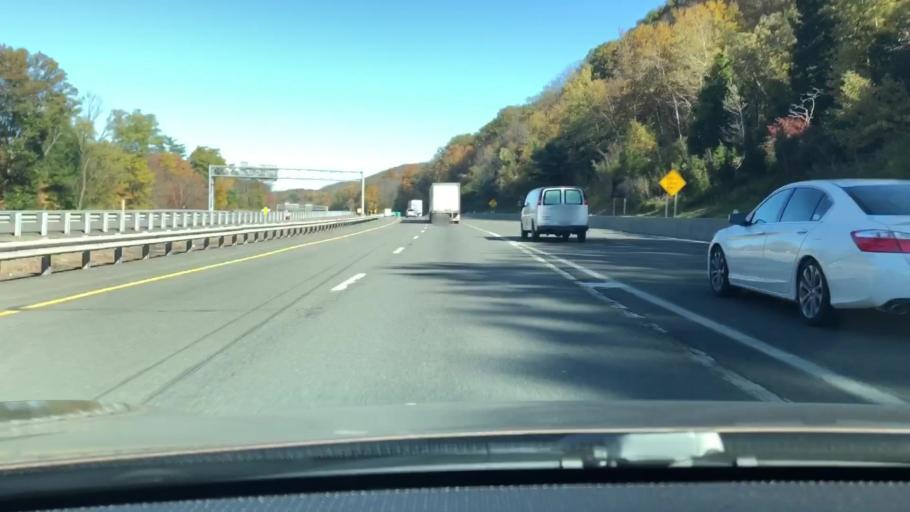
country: US
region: New York
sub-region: Orange County
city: Central Valley
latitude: 41.3136
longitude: -74.1182
